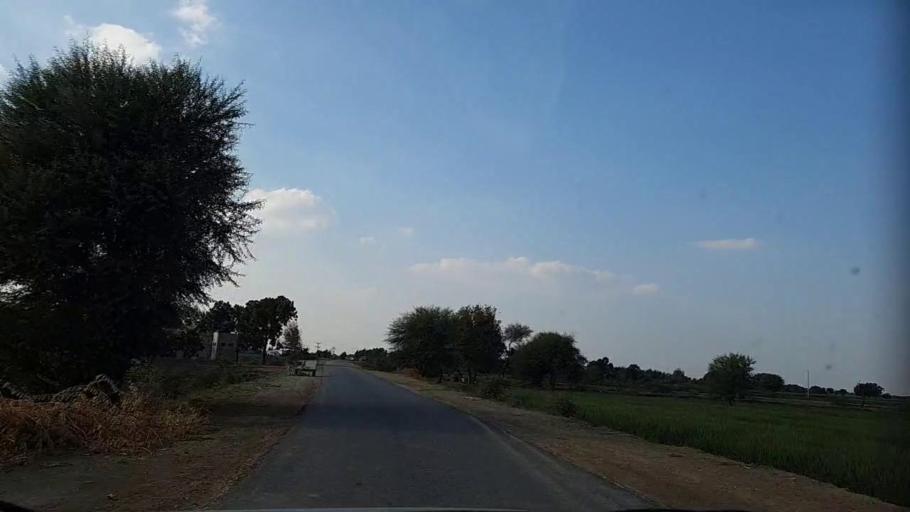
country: PK
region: Sindh
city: Pithoro
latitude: 25.6852
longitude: 69.2249
